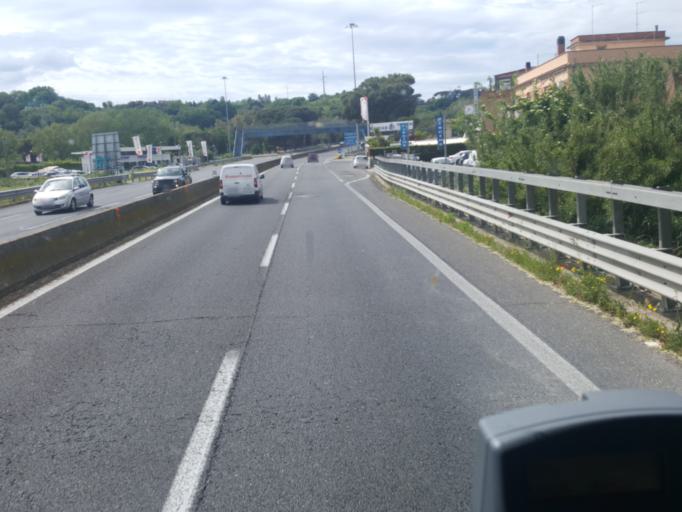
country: IT
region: Latium
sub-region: Citta metropolitana di Roma Capitale
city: Ara Nova
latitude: 41.9065
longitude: 12.2661
